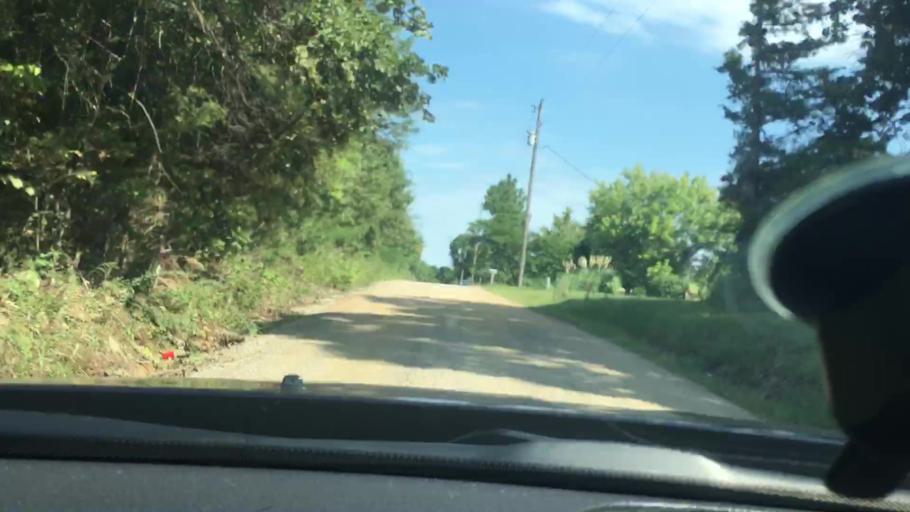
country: US
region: Texas
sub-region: Grayson County
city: Preston
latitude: 33.8910
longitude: -96.5627
